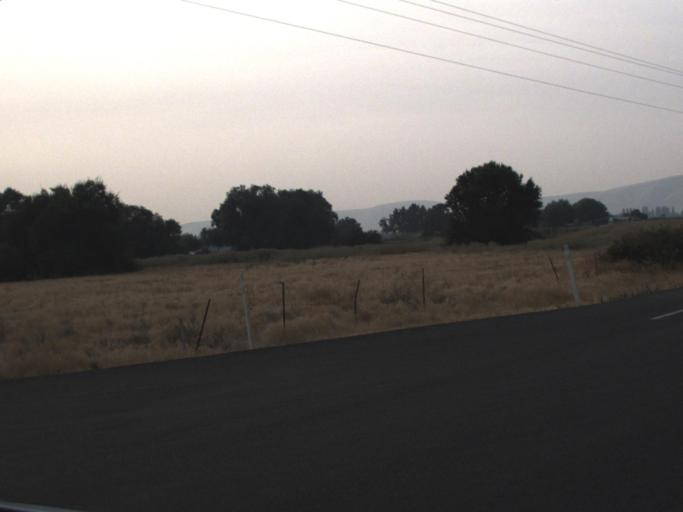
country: US
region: Washington
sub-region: Yakima County
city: Toppenish
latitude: 46.3604
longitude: -120.3202
